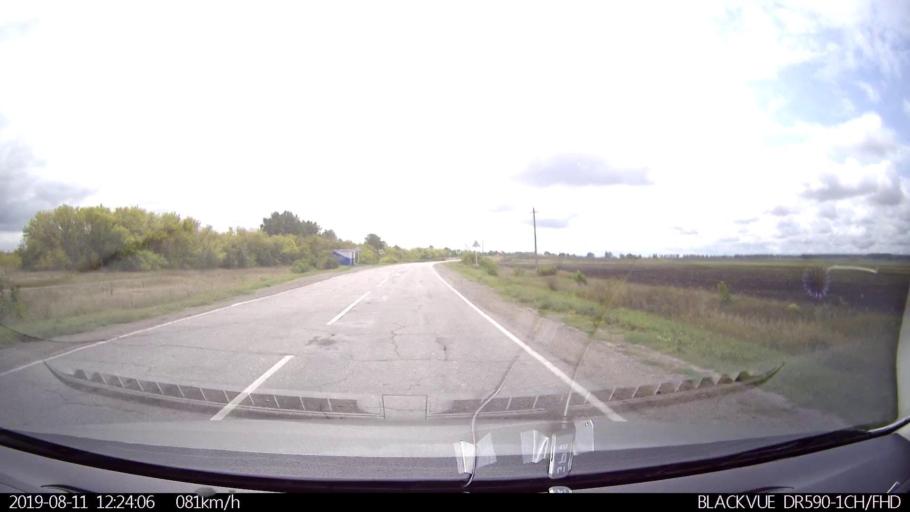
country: RU
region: Ulyanovsk
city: Ignatovka
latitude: 53.8872
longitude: 47.9500
